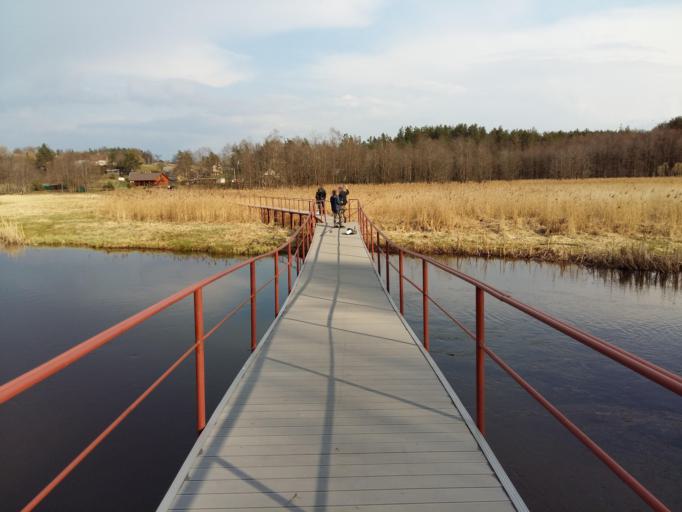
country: LT
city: Svencioneliai
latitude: 55.1568
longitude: 25.9845
